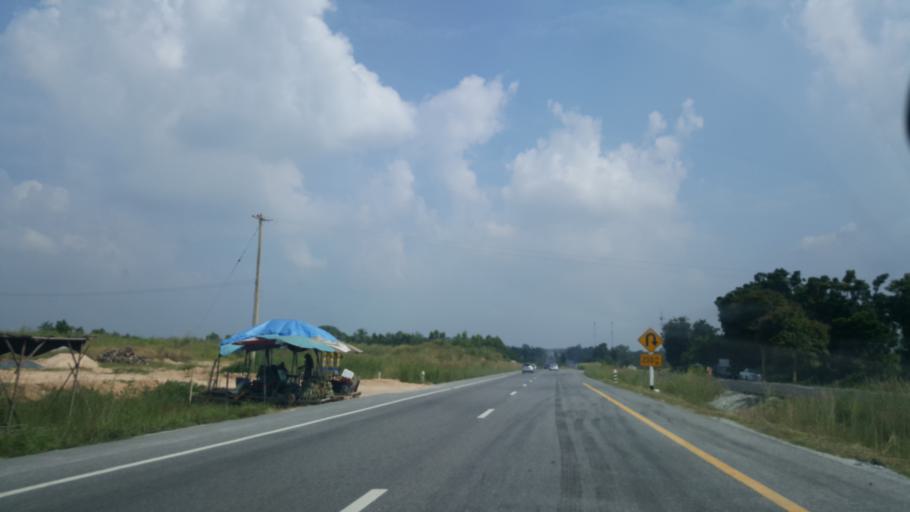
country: TH
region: Rayong
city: Ban Chang
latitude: 12.8340
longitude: 101.0070
